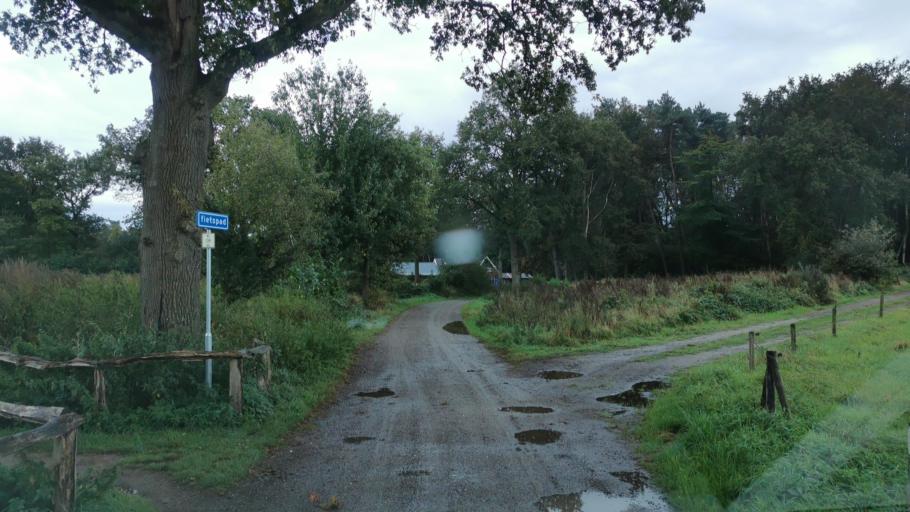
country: NL
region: Overijssel
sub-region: Gemeente Losser
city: Losser
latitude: 52.3056
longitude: 7.0283
